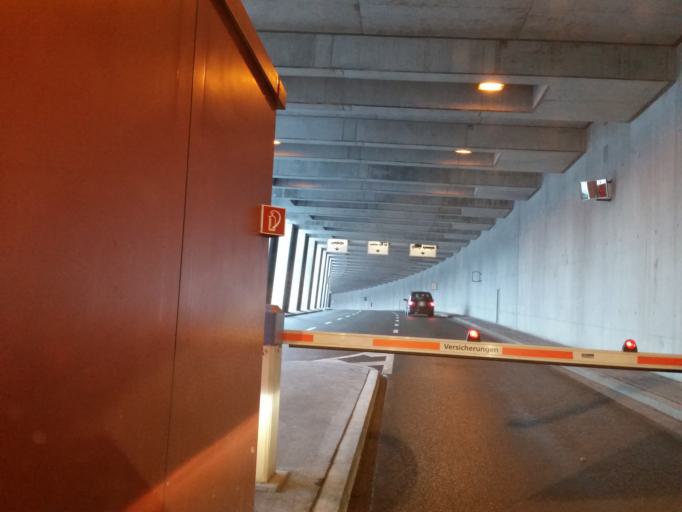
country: CH
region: Grisons
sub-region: Inn District
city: Zernez
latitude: 46.7646
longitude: 10.1011
